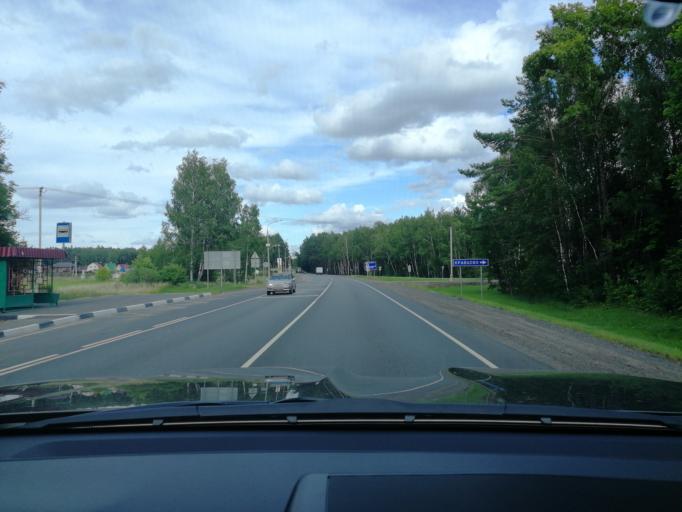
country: RU
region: Moskovskaya
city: Mikhnevo
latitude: 55.0705
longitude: 37.8452
